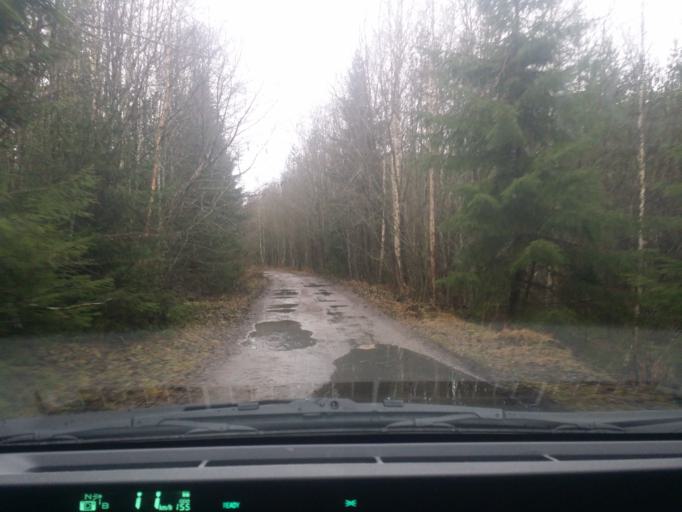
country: SE
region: Vaestmanland
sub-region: Norbergs Kommun
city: Norberg
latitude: 60.1120
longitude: 15.9710
